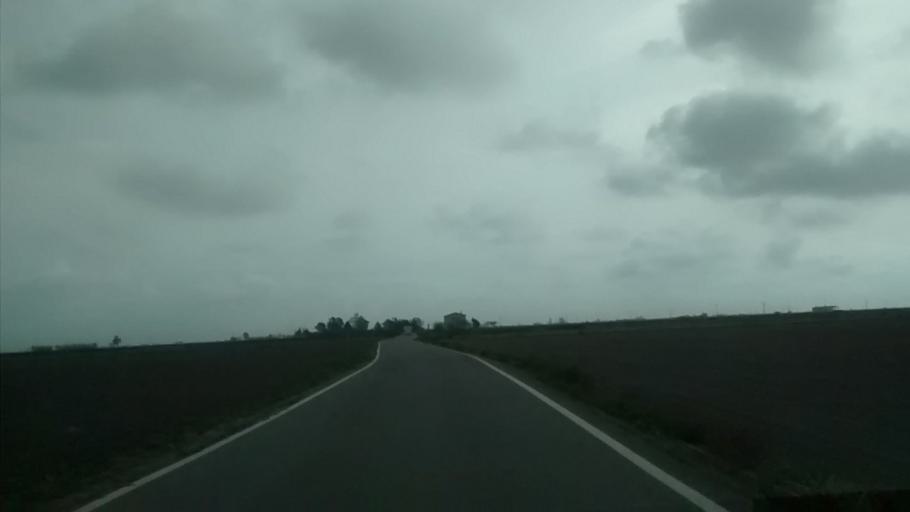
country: ES
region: Catalonia
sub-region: Provincia de Tarragona
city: Sant Carles de la Rapita
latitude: 40.6499
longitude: 0.6185
